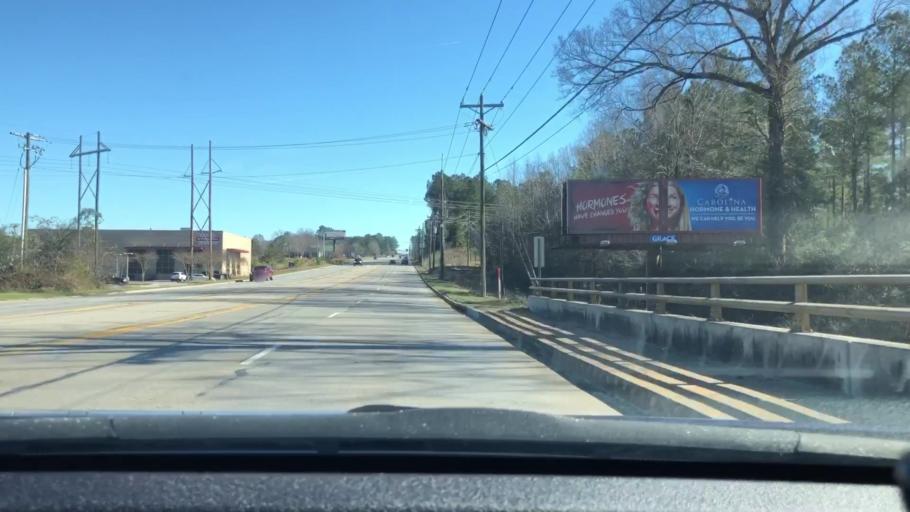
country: US
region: South Carolina
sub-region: Lexington County
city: Oak Grove
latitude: 34.0131
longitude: -81.1702
